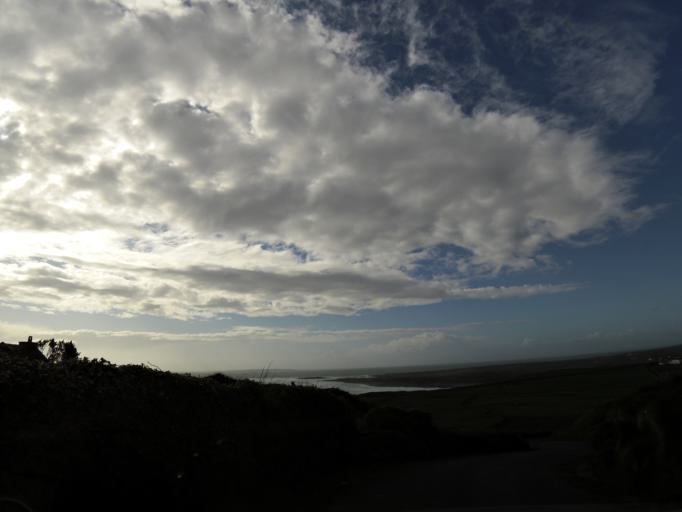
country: IE
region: Connaught
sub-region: County Galway
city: Bearna
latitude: 53.0035
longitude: -9.3886
